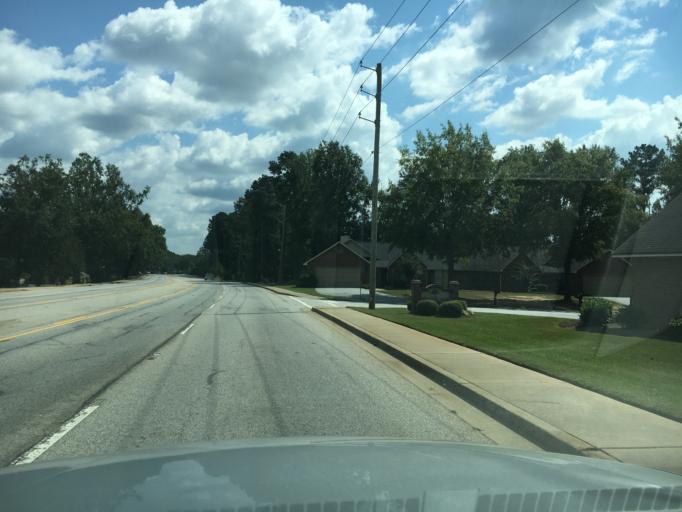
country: US
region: South Carolina
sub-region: Greenwood County
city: Greenwood
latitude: 34.1975
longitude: -82.1938
